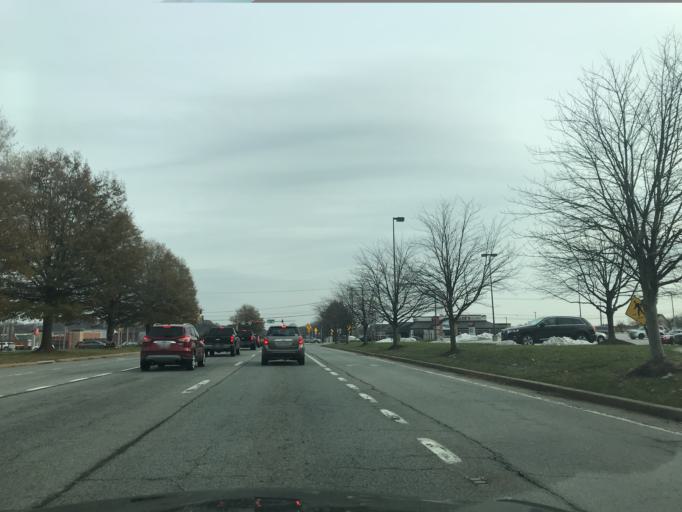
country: US
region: Maryland
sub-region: Harford County
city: Bel Air
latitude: 39.5270
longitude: -76.3558
